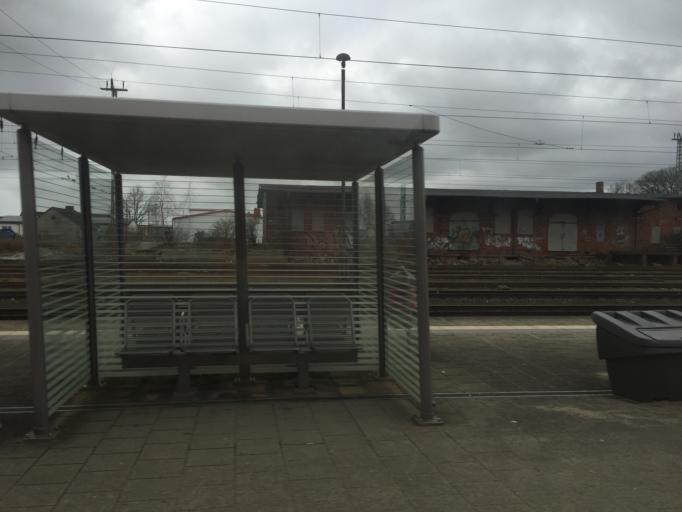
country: DE
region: Mecklenburg-Vorpommern
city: Bergen auf Ruegen
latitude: 54.4205
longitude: 13.4174
